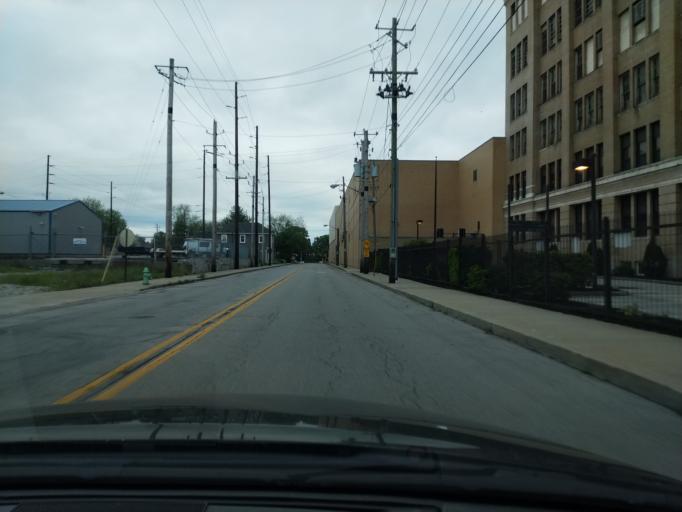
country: US
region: Indiana
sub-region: Marion County
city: Indianapolis
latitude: 39.7404
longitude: -86.1495
